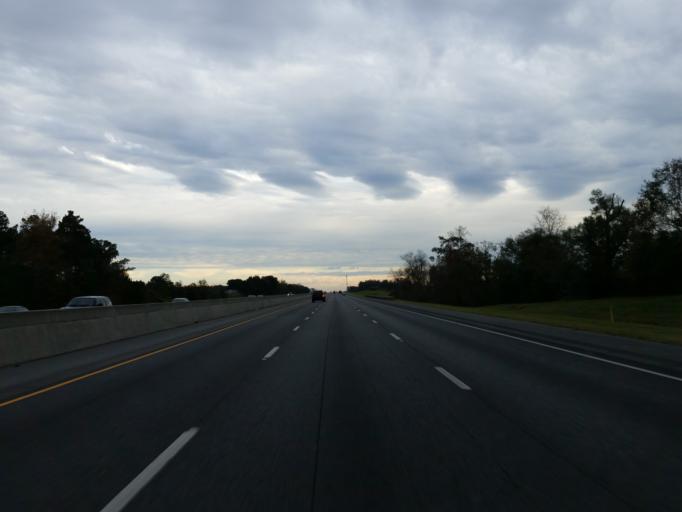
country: US
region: Georgia
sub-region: Lowndes County
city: Hahira
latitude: 30.9639
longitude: -83.3794
